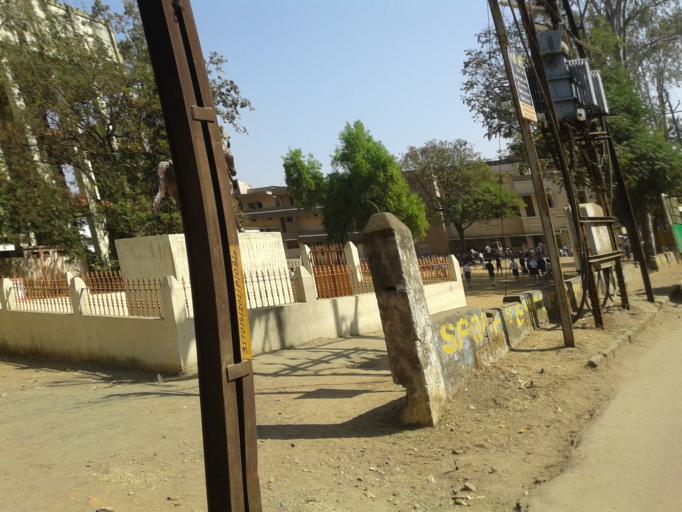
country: IN
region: Maharashtra
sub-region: Gondiya
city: Gondia
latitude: 21.4637
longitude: 80.1948
